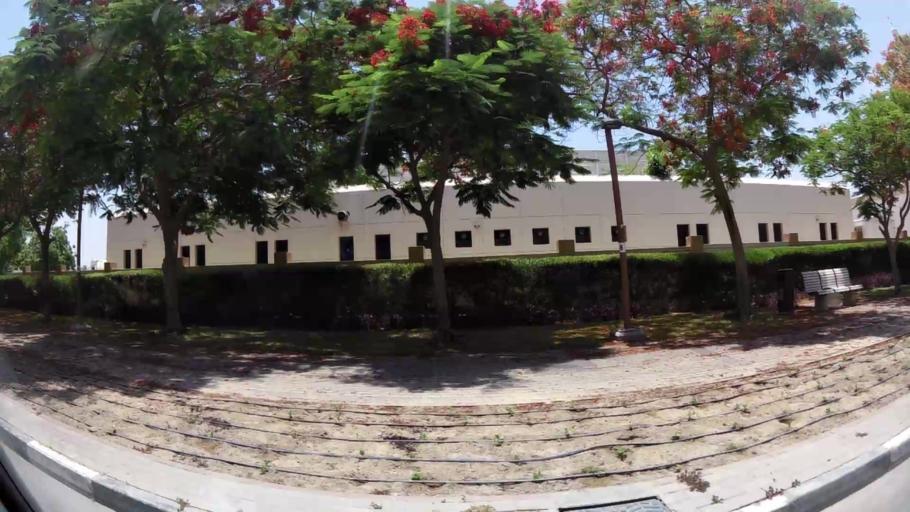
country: AE
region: Ash Shariqah
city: Sharjah
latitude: 25.2837
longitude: 55.3195
